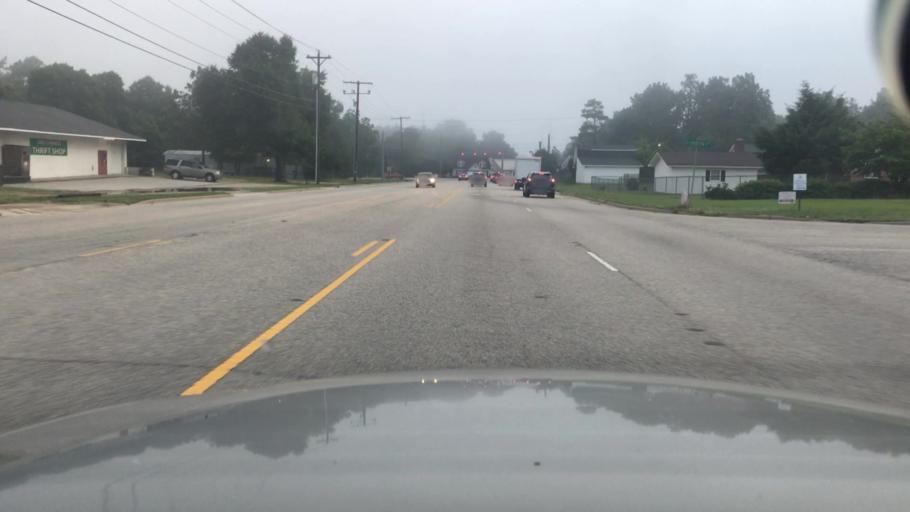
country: US
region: North Carolina
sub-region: Cumberland County
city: Hope Mills
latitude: 35.0162
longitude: -78.9187
